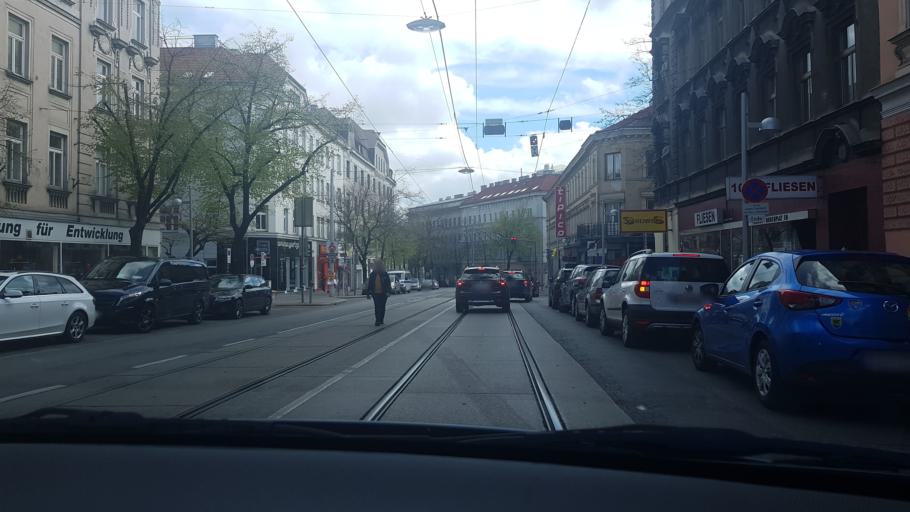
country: AT
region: Vienna
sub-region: Wien Stadt
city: Vienna
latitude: 48.1989
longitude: 16.3231
